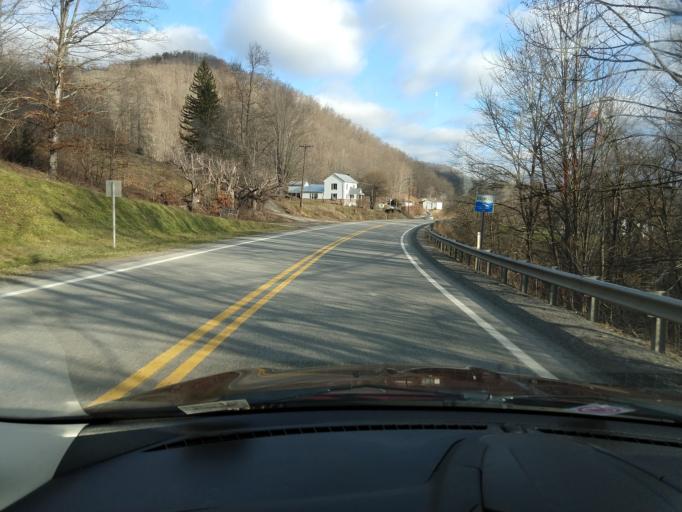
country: US
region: West Virginia
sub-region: Randolph County
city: Elkins
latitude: 38.7547
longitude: -79.9568
